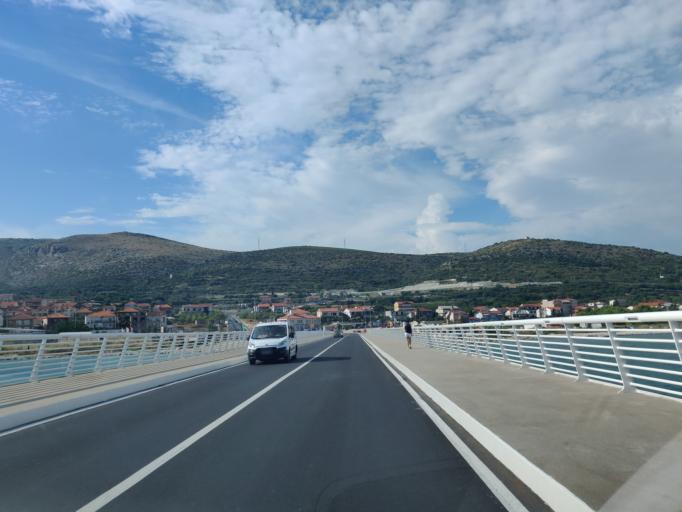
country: HR
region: Splitsko-Dalmatinska
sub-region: Grad Trogir
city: Trogir
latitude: 43.5198
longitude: 16.2649
